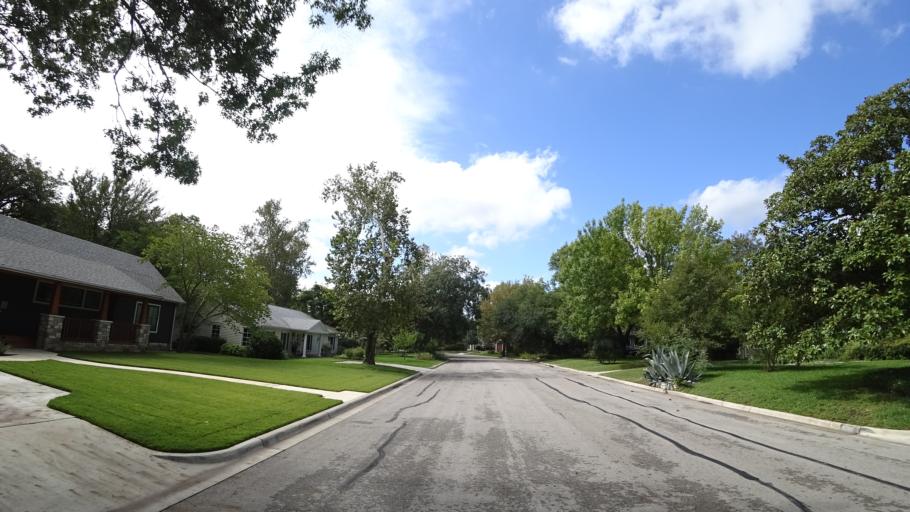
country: US
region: Texas
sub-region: Travis County
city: West Lake Hills
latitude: 30.3391
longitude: -97.7433
